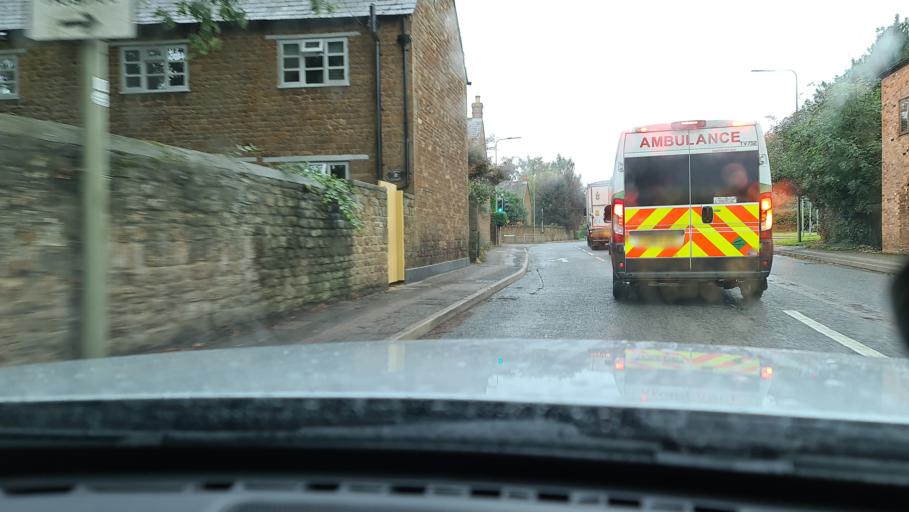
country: GB
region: England
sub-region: Oxfordshire
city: Adderbury
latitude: 52.0183
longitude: -1.3106
